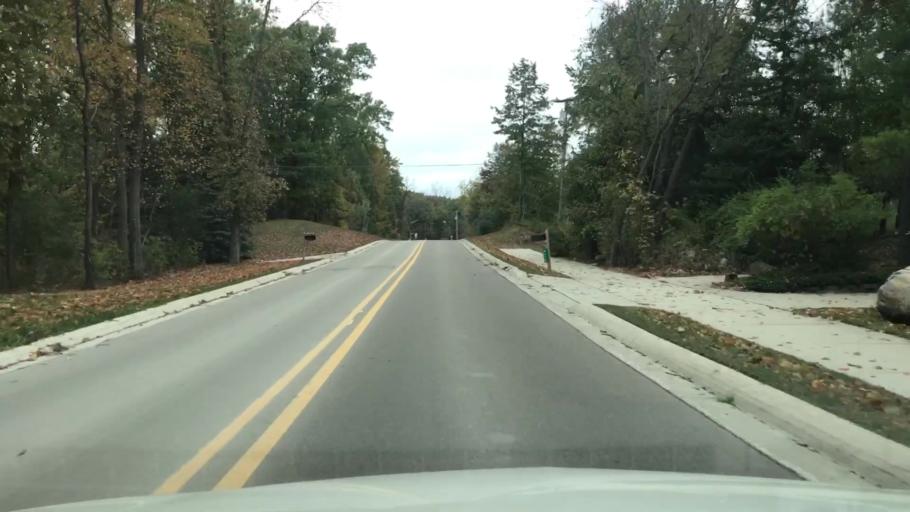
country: US
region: Michigan
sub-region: Oakland County
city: Rochester
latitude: 42.7090
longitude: -83.1248
